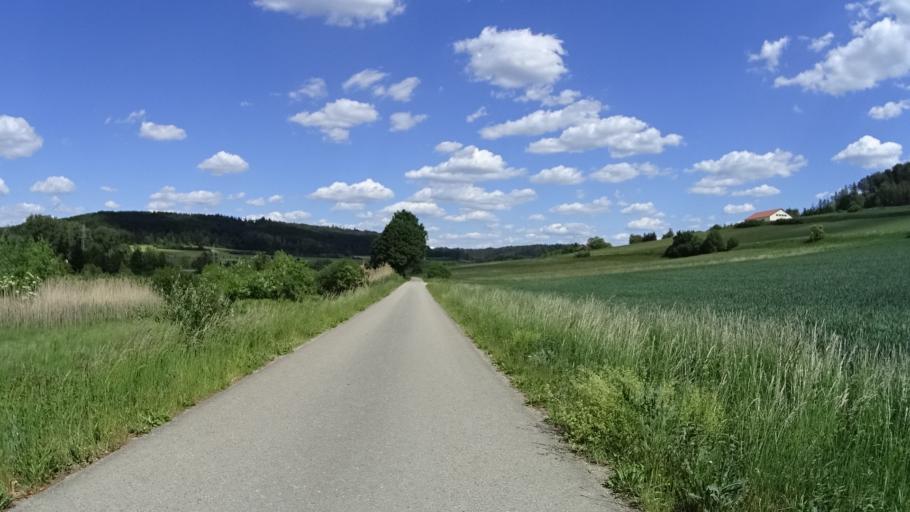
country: DE
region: Bavaria
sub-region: Regierungsbezirk Mittelfranken
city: Greding
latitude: 49.0634
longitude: 11.3124
